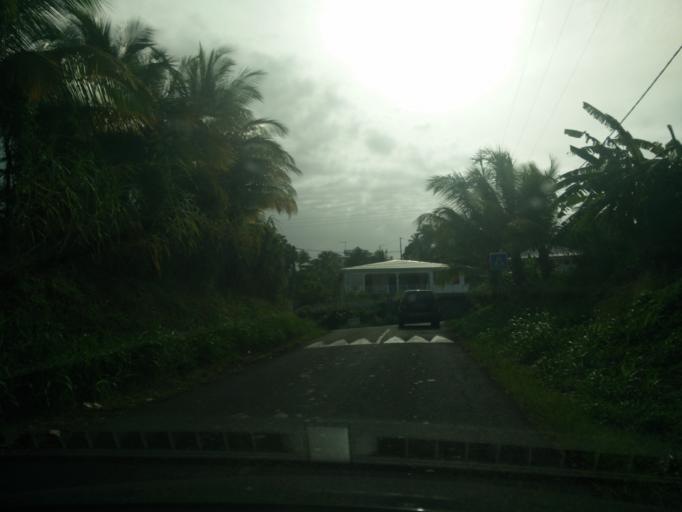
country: GP
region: Guadeloupe
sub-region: Guadeloupe
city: Petit-Bourg
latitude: 16.1270
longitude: -61.5932
